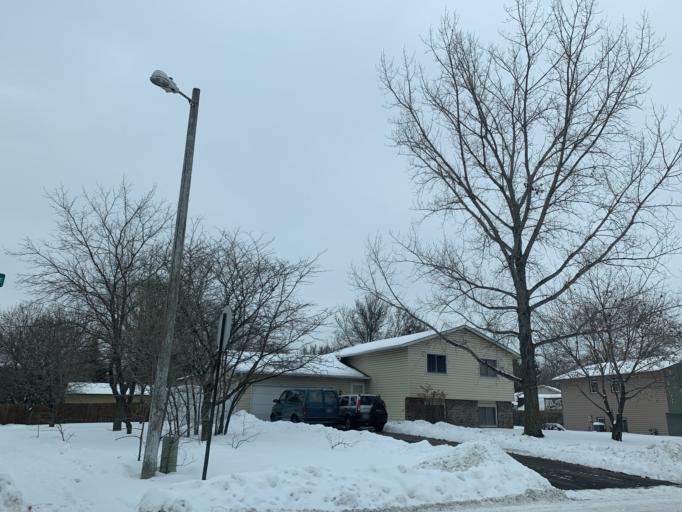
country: US
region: Minnesota
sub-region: Anoka County
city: Coon Rapids
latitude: 45.1648
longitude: -93.2995
